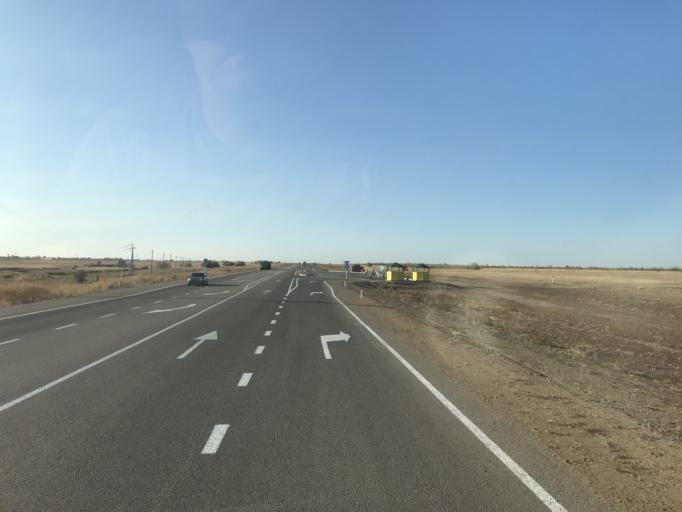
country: KZ
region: Pavlodar
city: Koktobe
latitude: 51.8819
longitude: 77.4204
